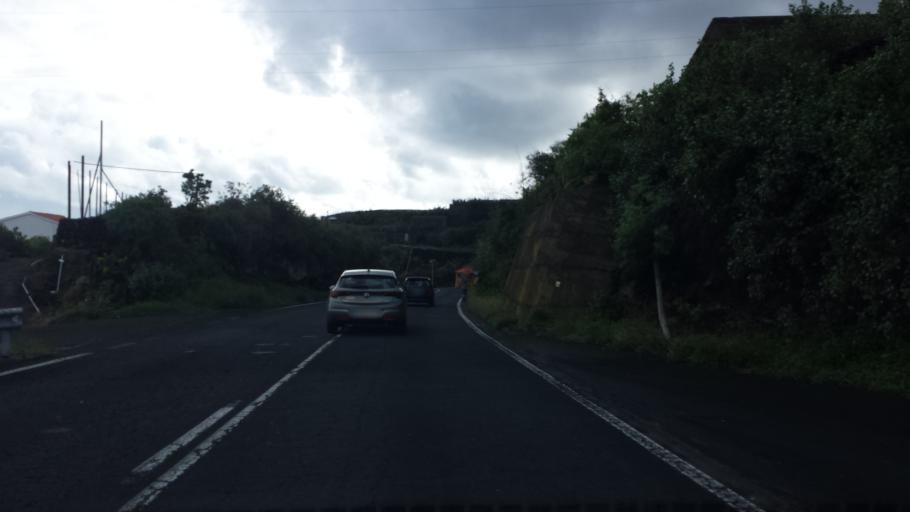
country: ES
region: Canary Islands
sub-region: Provincia de Santa Cruz de Tenerife
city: Brena Alta
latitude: 28.6599
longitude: -17.7710
